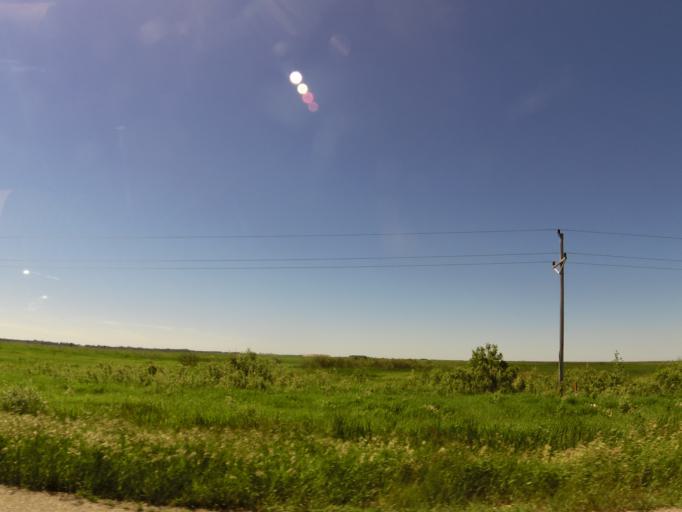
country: US
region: Minnesota
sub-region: Red Lake County
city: Red Lake Falls
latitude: 47.7600
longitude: -96.3013
